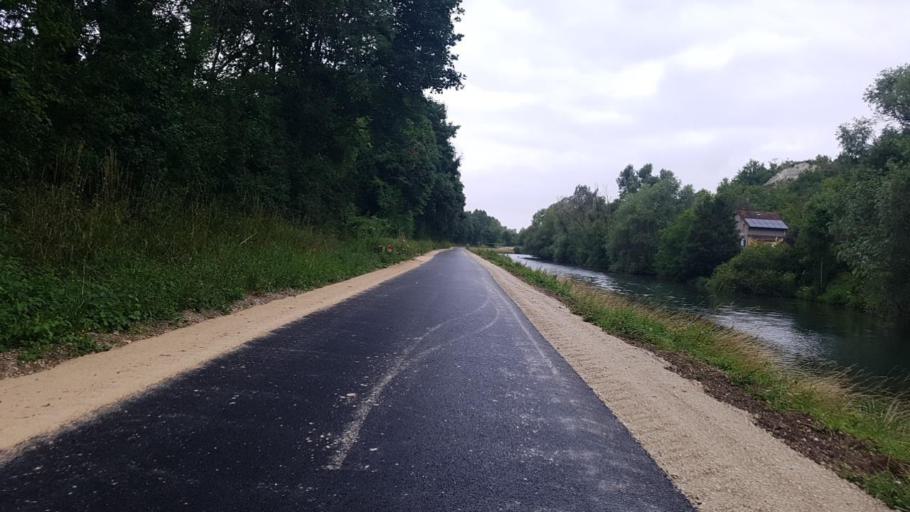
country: FR
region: Champagne-Ardenne
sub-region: Departement de la Marne
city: Vitry-le-Francois
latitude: 48.7603
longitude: 4.5657
